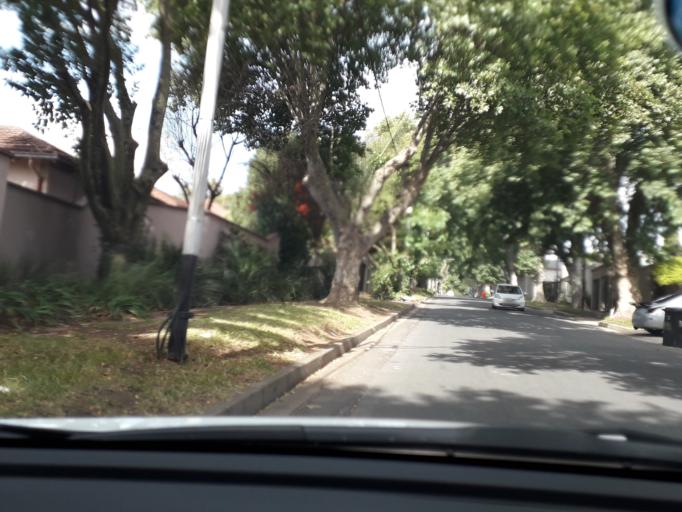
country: ZA
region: Gauteng
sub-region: City of Johannesburg Metropolitan Municipality
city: Johannesburg
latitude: -26.1555
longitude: 28.0717
